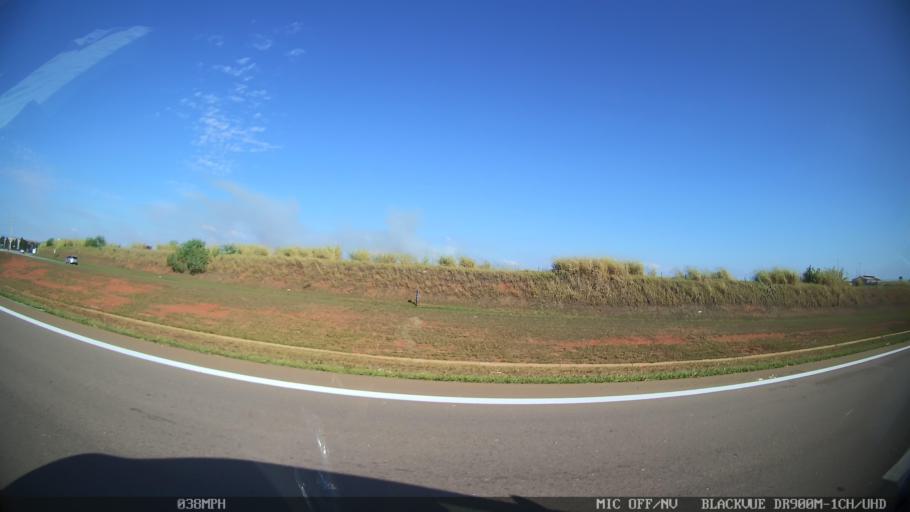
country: BR
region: Sao Paulo
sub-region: Piracicaba
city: Piracicaba
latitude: -22.6620
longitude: -47.6119
